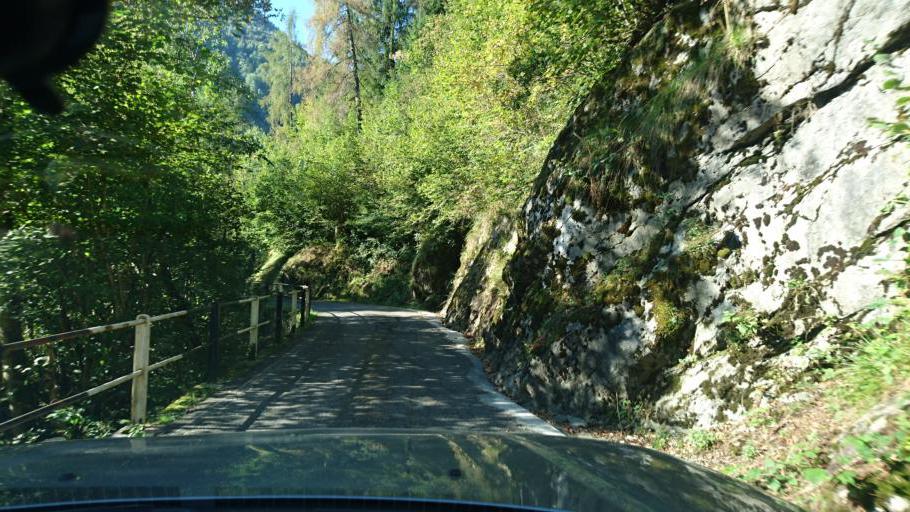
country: IT
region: Lombardy
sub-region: Provincia di Brescia
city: Paisco Loveno
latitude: 46.0638
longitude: 10.2536
